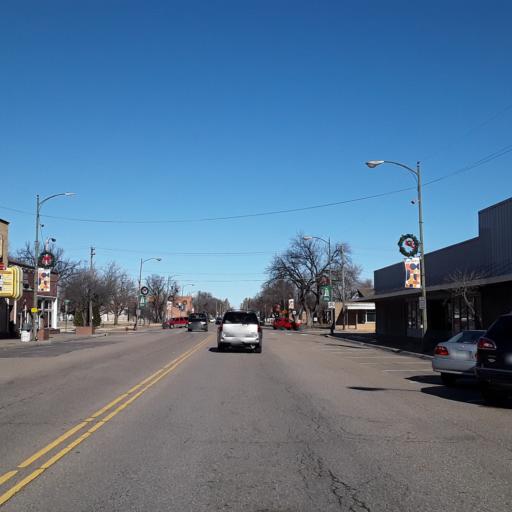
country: US
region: Kansas
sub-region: Pawnee County
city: Larned
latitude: 38.1803
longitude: -99.0984
